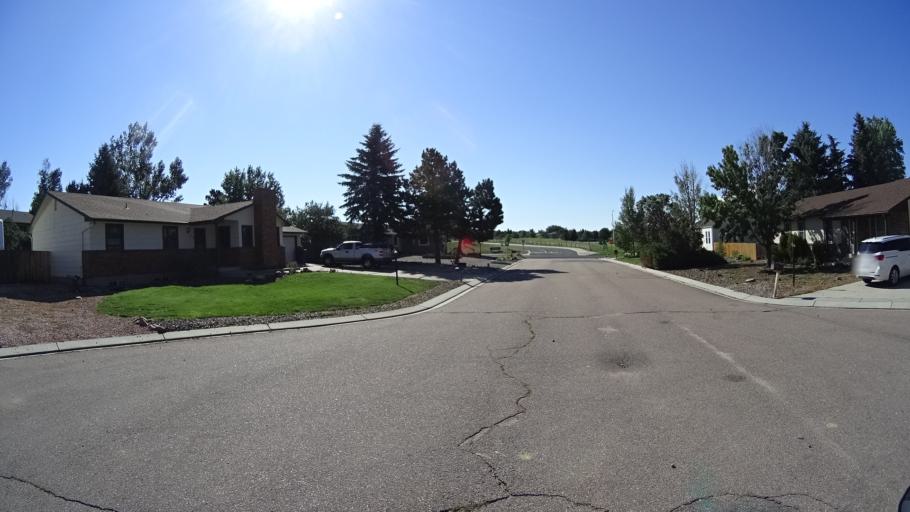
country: US
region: Colorado
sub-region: El Paso County
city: Gleneagle
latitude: 38.9775
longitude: -104.7782
